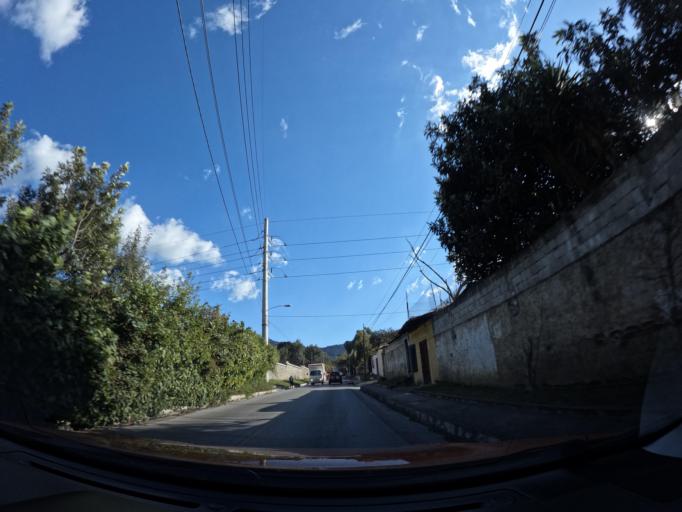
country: GT
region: Sacatepequez
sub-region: Municipio de Santa Maria de Jesus
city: Santa Maria de Jesus
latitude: 14.5327
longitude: -90.7282
